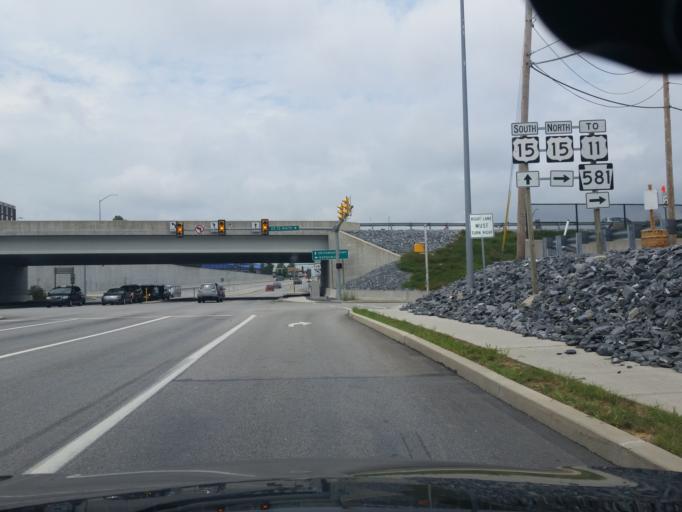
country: US
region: Pennsylvania
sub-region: Cumberland County
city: Shiremanstown
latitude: 40.2216
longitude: -76.9359
